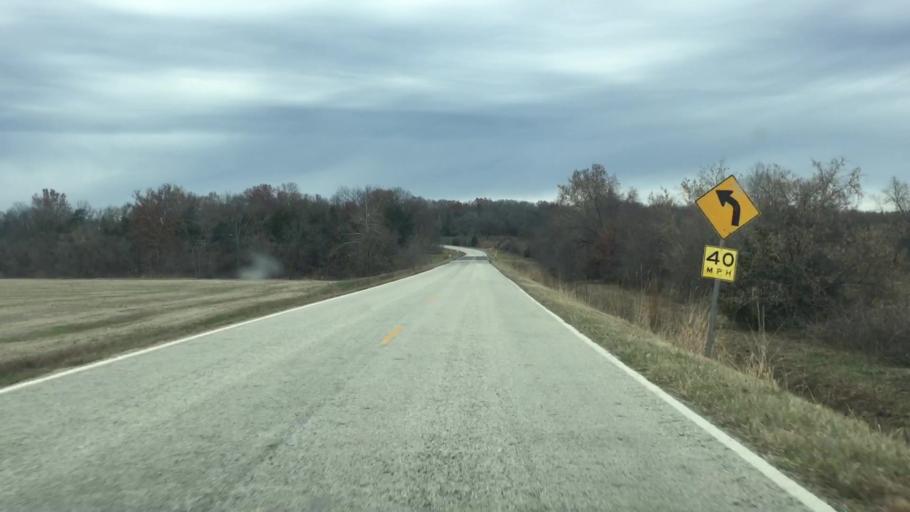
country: US
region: Missouri
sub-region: Saint Clair County
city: Osceola
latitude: 37.9842
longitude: -93.6118
